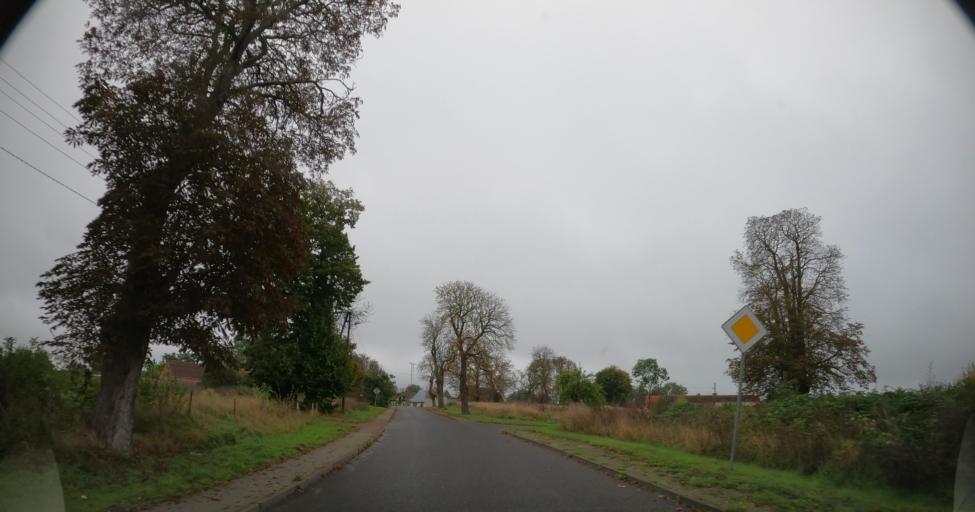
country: PL
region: West Pomeranian Voivodeship
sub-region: Powiat pyrzycki
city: Kozielice
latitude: 53.0937
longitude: 14.7684
